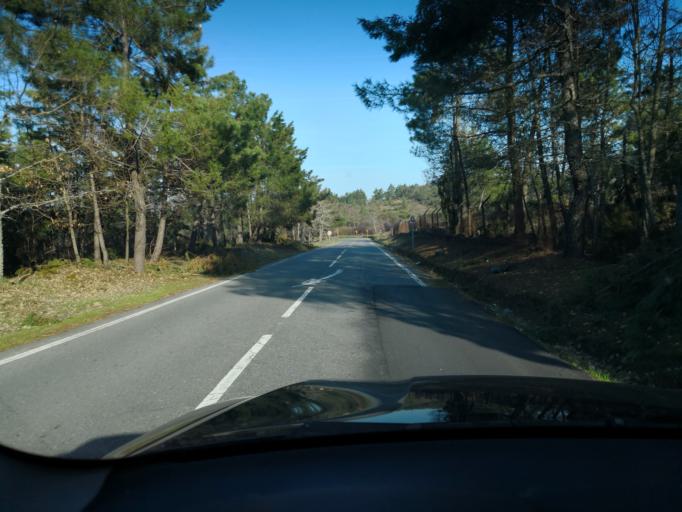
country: PT
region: Vila Real
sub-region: Sabrosa
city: Sabrosa
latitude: 41.3576
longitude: -7.6292
